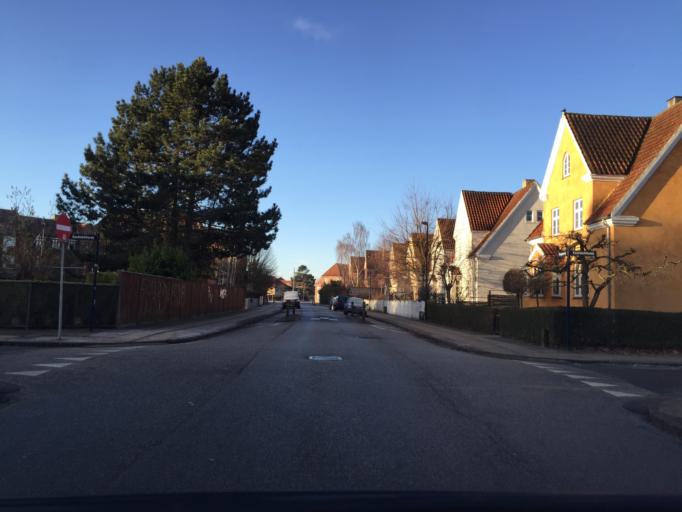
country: DK
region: Capital Region
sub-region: Kobenhavn
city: Vanlose
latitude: 55.6623
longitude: 12.5062
